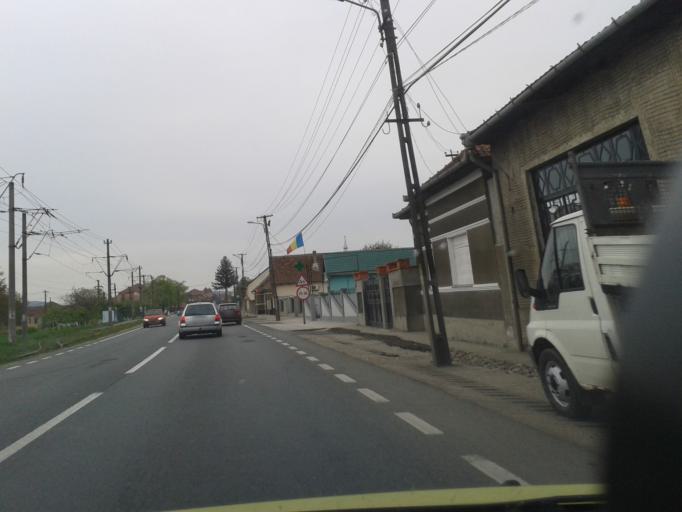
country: RO
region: Arad
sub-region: Comuna Paulis
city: Sambateni
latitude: 46.1413
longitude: 21.5219
